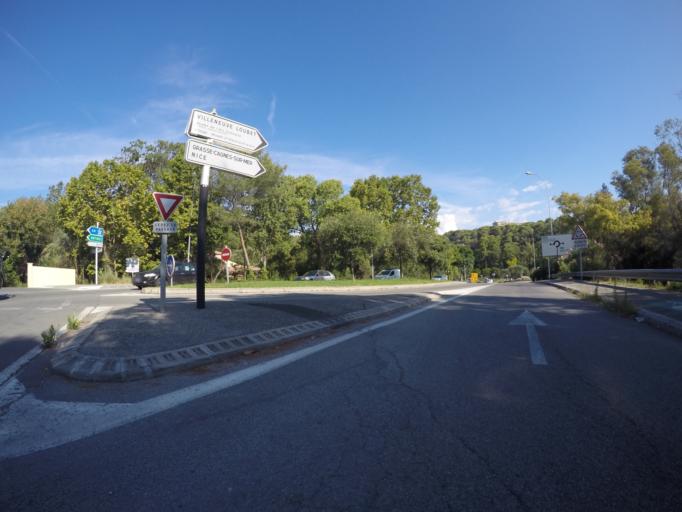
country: FR
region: Provence-Alpes-Cote d'Azur
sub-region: Departement des Alpes-Maritimes
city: Cagnes-sur-Mer
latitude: 43.6472
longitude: 7.1367
